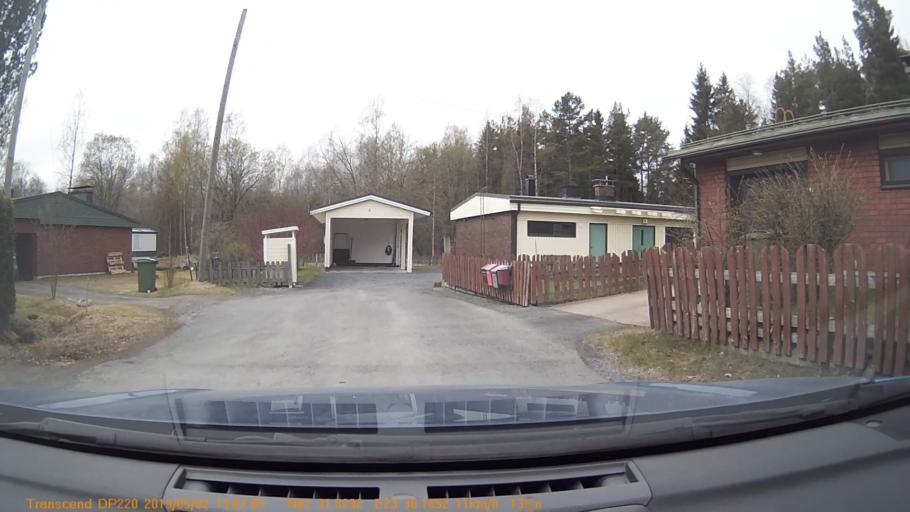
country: FI
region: Pirkanmaa
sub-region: Tampere
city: Yloejaervi
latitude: 61.5255
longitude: 23.6028
